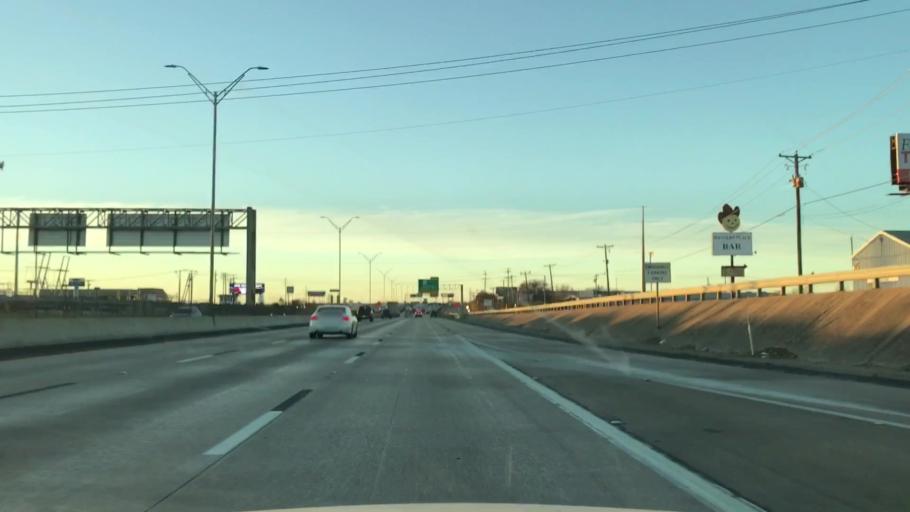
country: US
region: Texas
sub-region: Johnson County
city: Burleson
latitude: 32.5609
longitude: -97.3190
